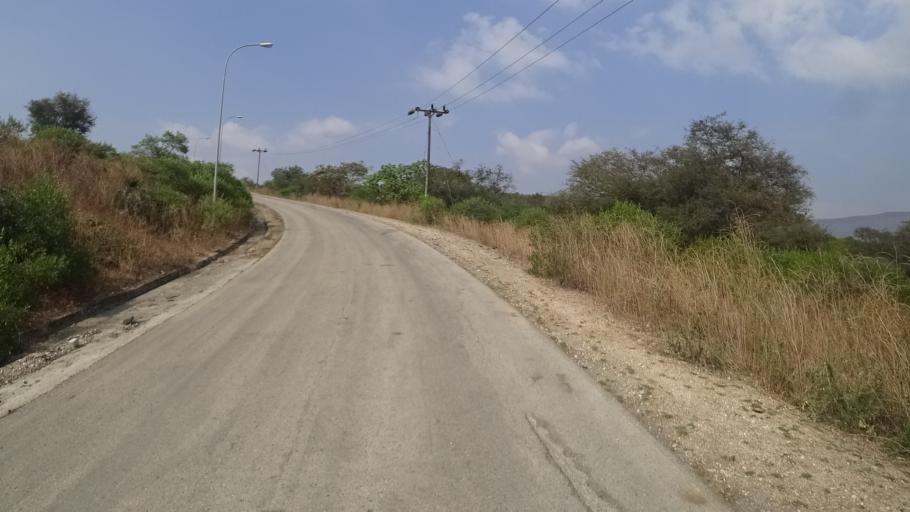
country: YE
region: Al Mahrah
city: Hawf
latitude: 16.7277
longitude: 53.2755
